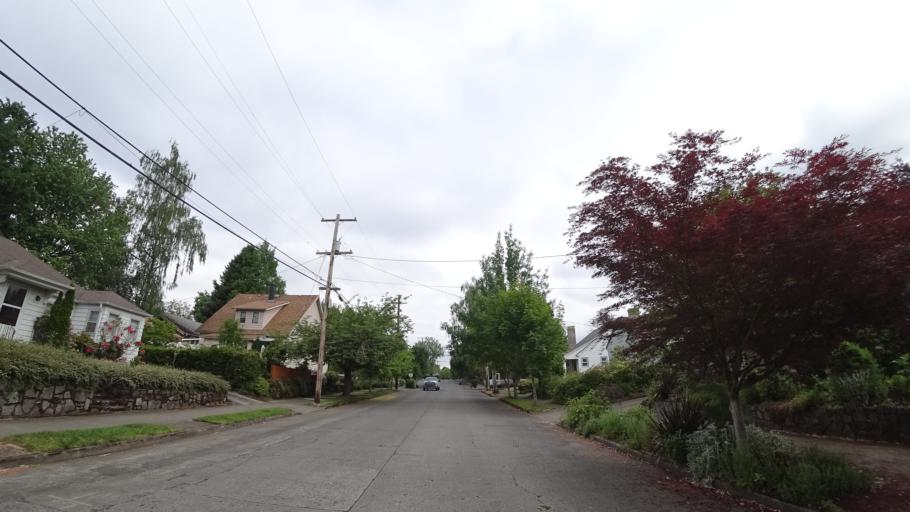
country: US
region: Oregon
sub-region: Multnomah County
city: Portland
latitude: 45.4992
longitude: -122.6315
